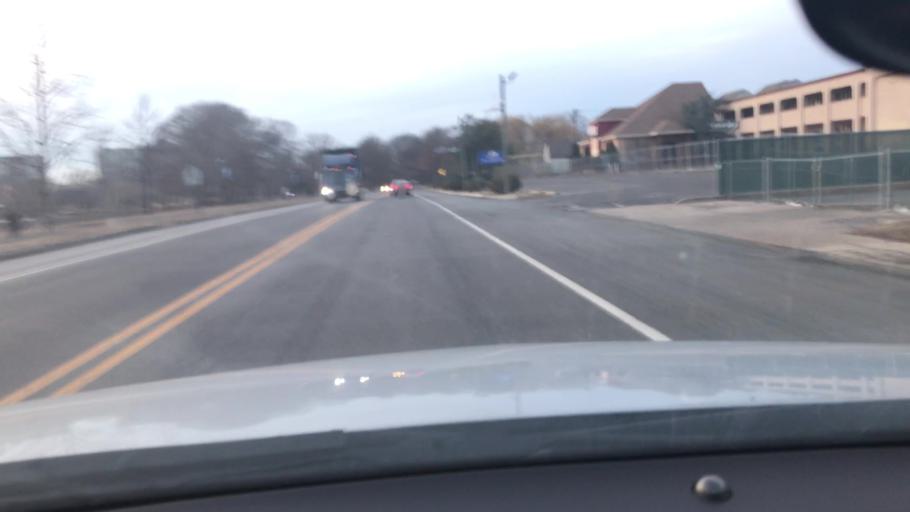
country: US
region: New Jersey
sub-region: Camden County
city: Collingswood
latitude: 39.9276
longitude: -75.0595
